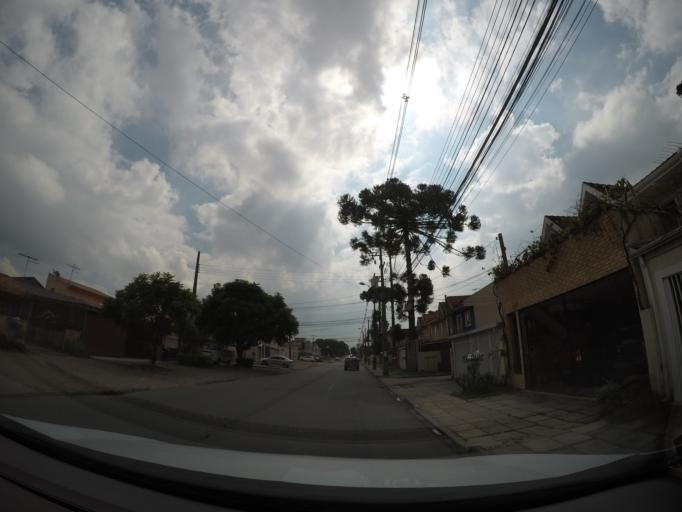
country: BR
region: Parana
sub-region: Sao Jose Dos Pinhais
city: Sao Jose dos Pinhais
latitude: -25.5027
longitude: -49.2494
